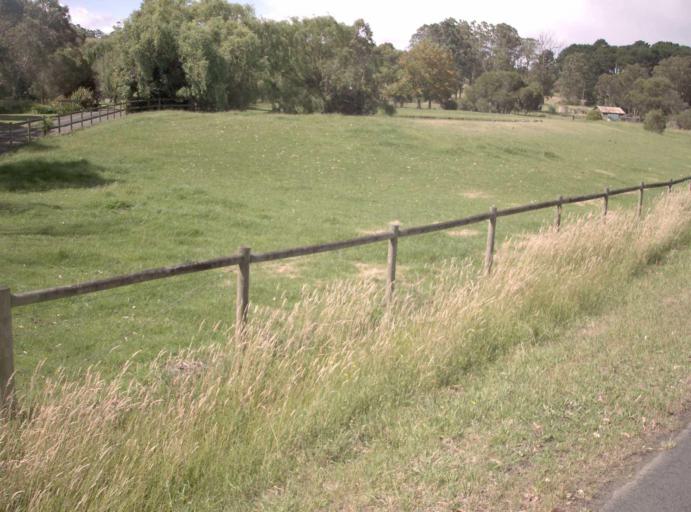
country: AU
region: Victoria
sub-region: Latrobe
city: Morwell
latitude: -38.1624
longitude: 146.4049
